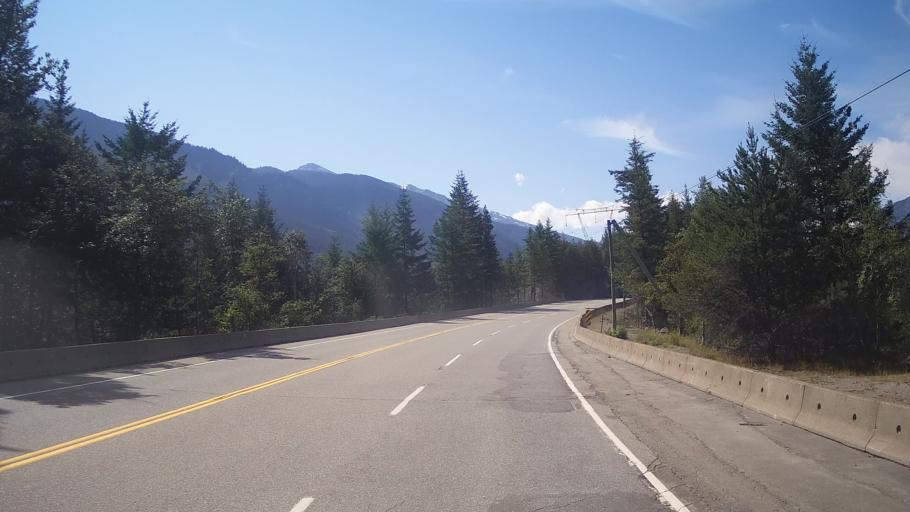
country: CA
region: British Columbia
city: Pemberton
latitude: 50.2542
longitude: -122.8600
